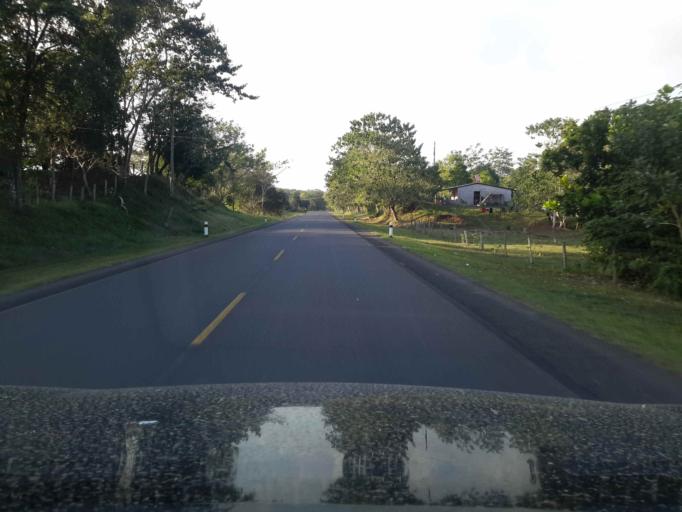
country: NI
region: Rio San Juan
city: San Carlos
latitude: 11.2890
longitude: -84.7230
